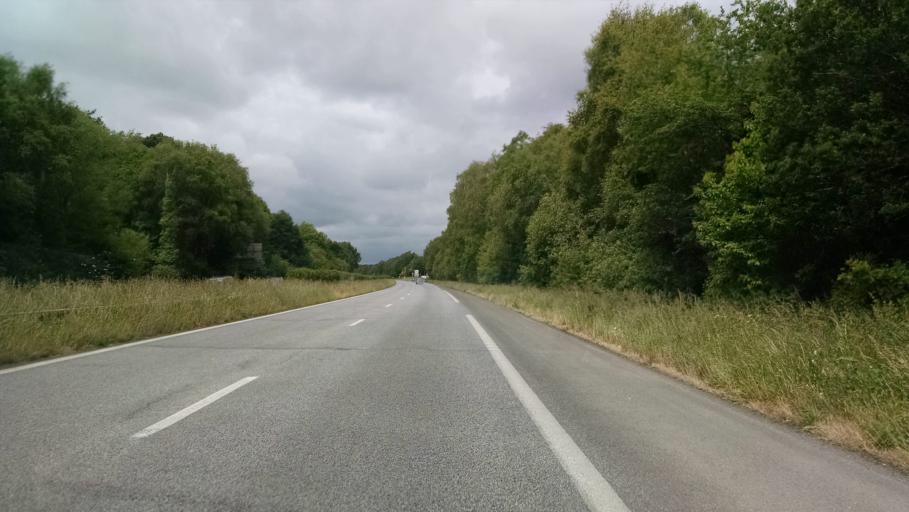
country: FR
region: Brittany
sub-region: Departement du Morbihan
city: Gestel
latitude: 47.8170
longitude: -3.4639
